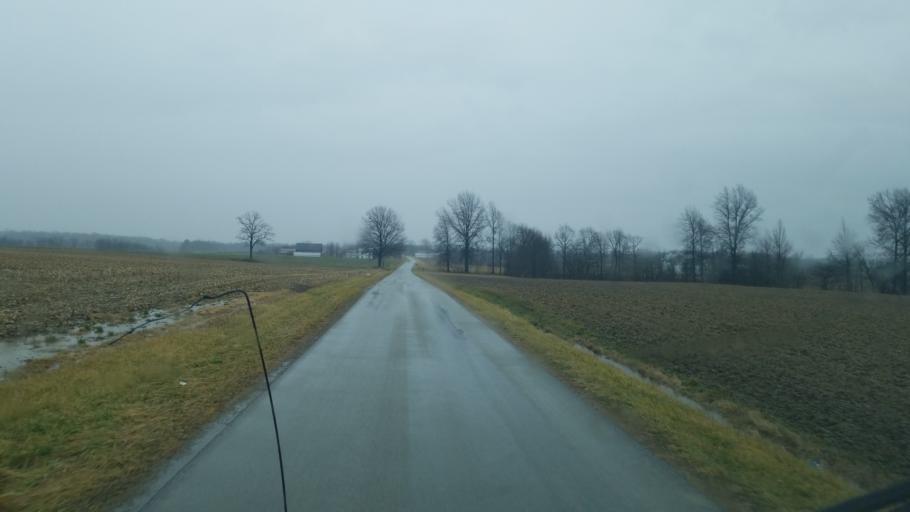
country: US
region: Ohio
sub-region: Hardin County
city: Forest
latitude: 40.7594
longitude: -83.3967
